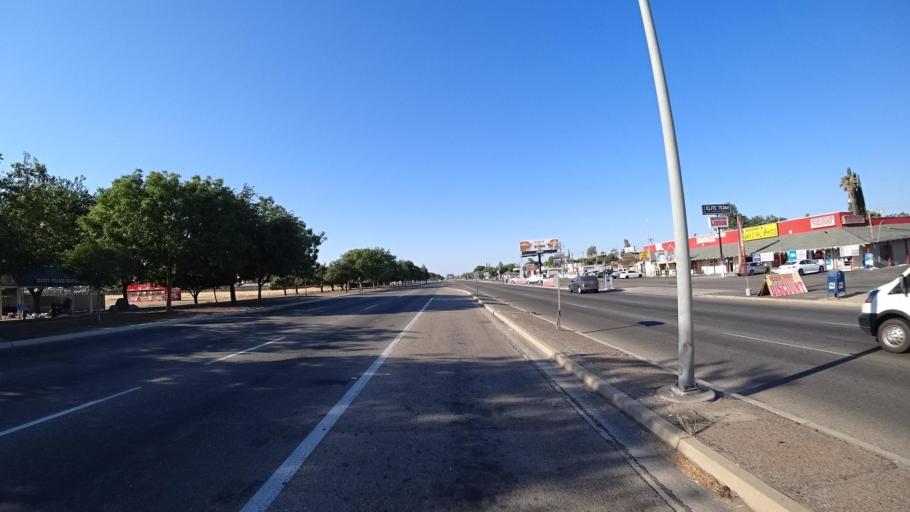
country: US
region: California
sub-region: Fresno County
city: Tarpey Village
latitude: 36.7928
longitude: -119.7003
